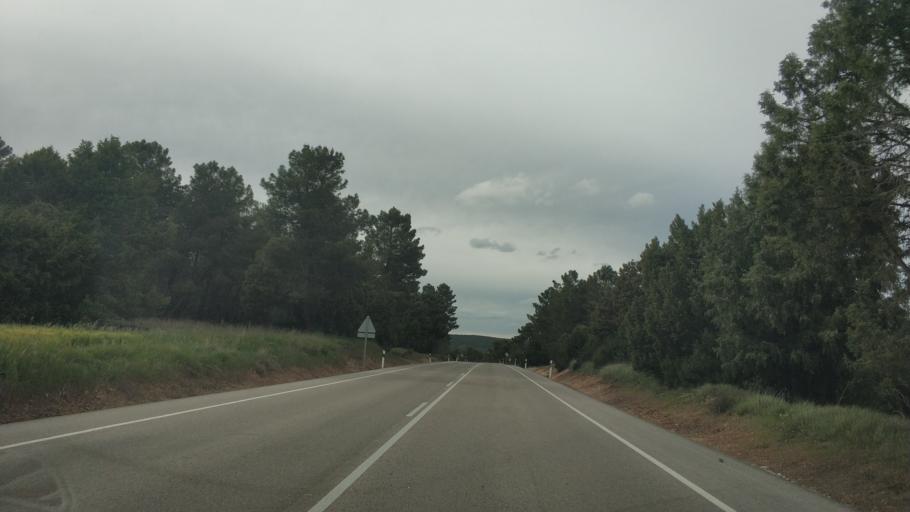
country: ES
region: Castille and Leon
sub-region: Provincia de Soria
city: Valdenebro
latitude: 41.5506
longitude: -2.9621
